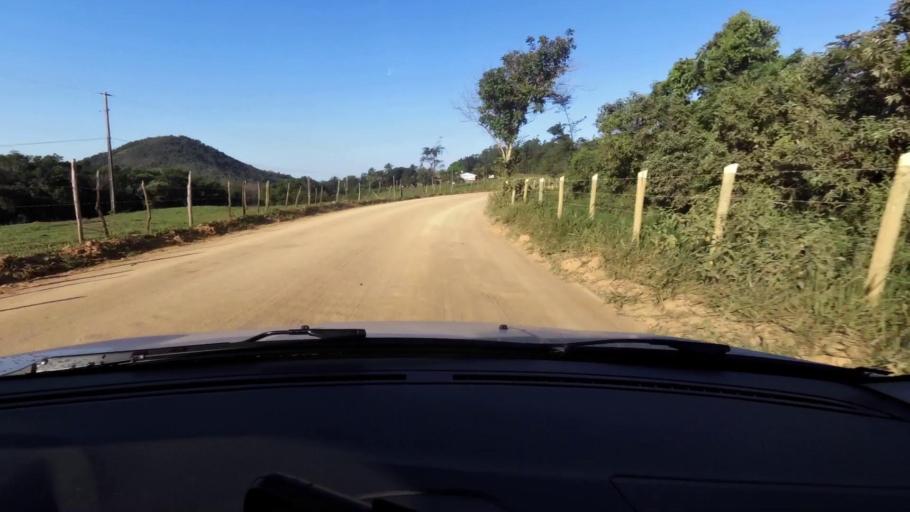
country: BR
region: Espirito Santo
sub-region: Guarapari
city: Guarapari
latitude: -20.7235
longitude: -40.5838
